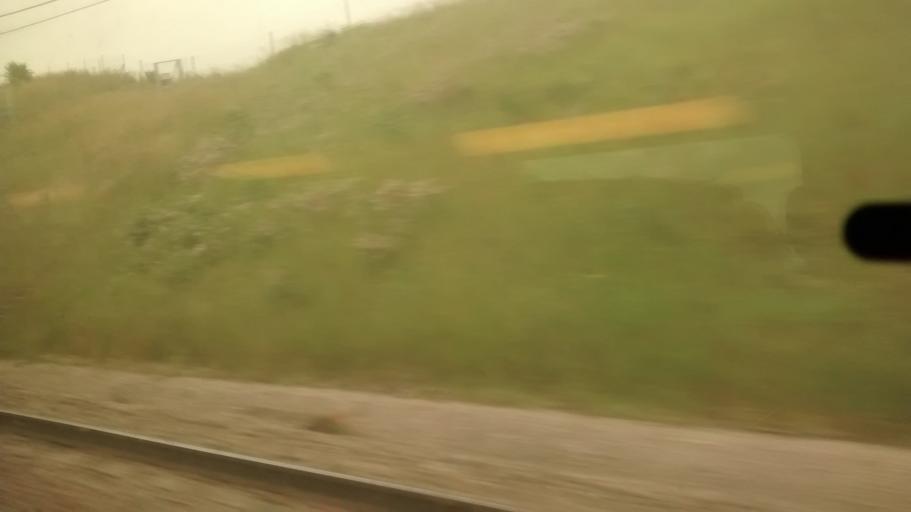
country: FR
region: Bourgogne
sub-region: Departement de l'Yonne
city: Courlon-sur-Yonne
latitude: 48.3431
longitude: 3.1916
